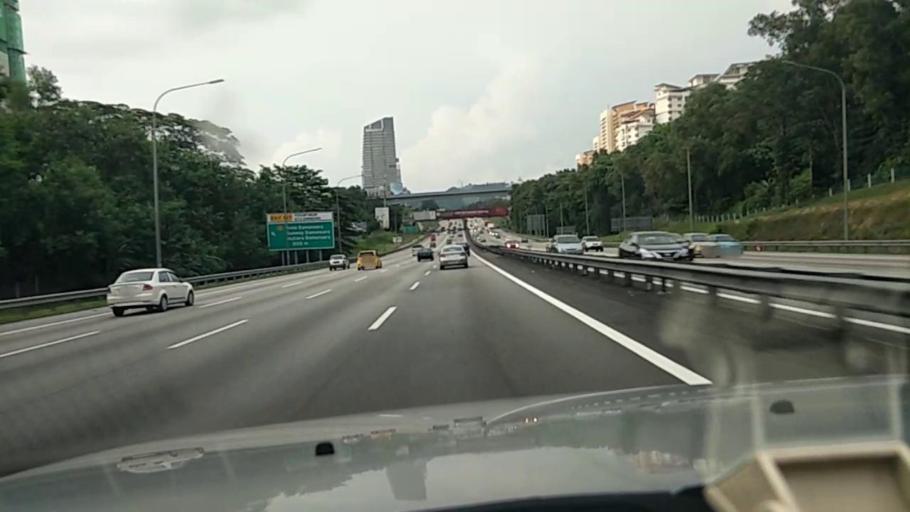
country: MY
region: Selangor
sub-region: Petaling
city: Petaling Jaya
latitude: 3.1453
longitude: 101.5968
